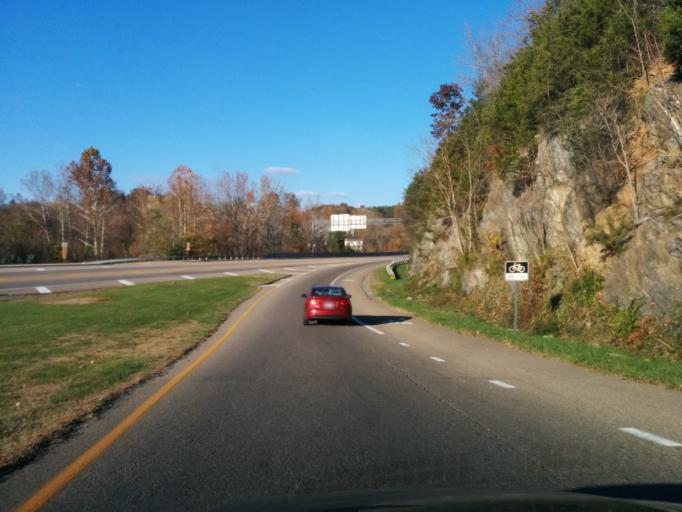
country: US
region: Virginia
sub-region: Rockbridge County
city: East Lexington
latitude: 37.7903
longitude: -79.4286
